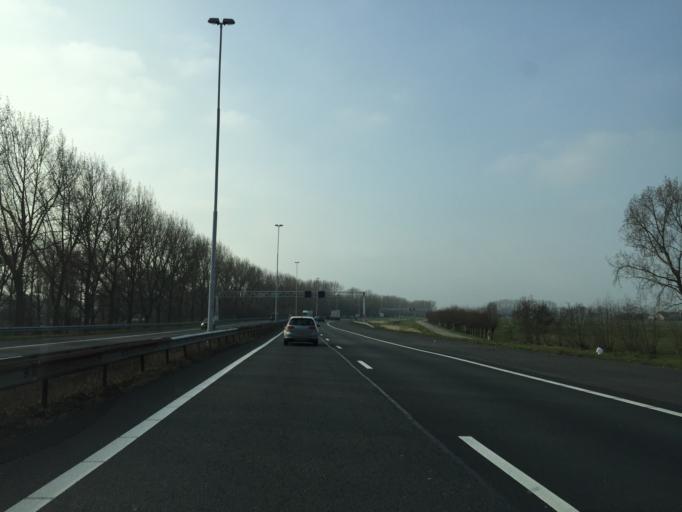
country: NL
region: South Holland
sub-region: Gemeente Maassluis
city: Maassluis
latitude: 51.9270
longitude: 4.2630
